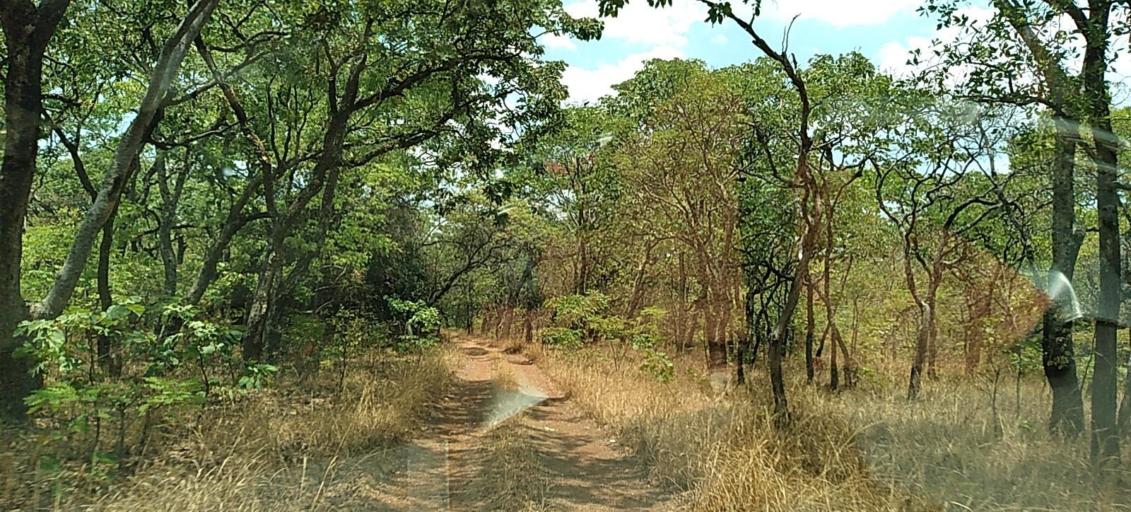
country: ZM
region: Copperbelt
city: Chililabombwe
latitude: -12.4517
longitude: 27.6971
